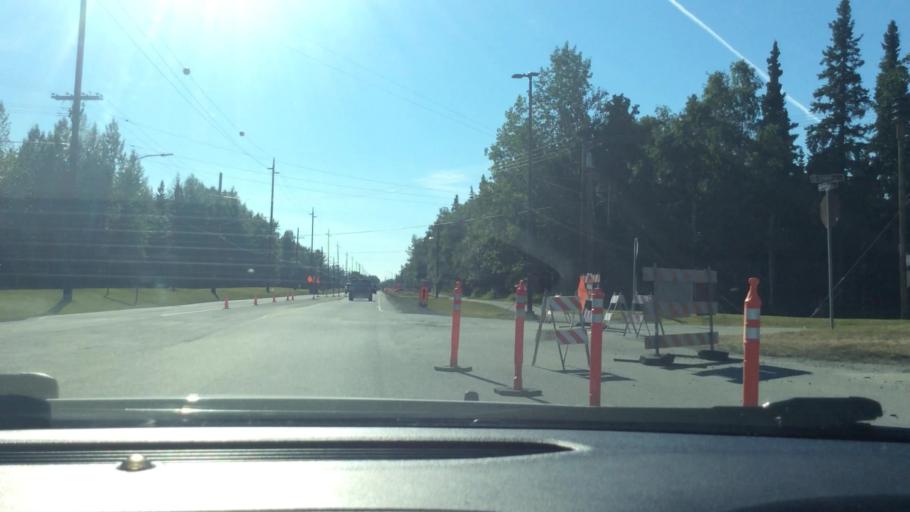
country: US
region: Alaska
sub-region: Anchorage Municipality
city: Elmendorf Air Force Base
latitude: 61.2314
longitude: -149.7484
